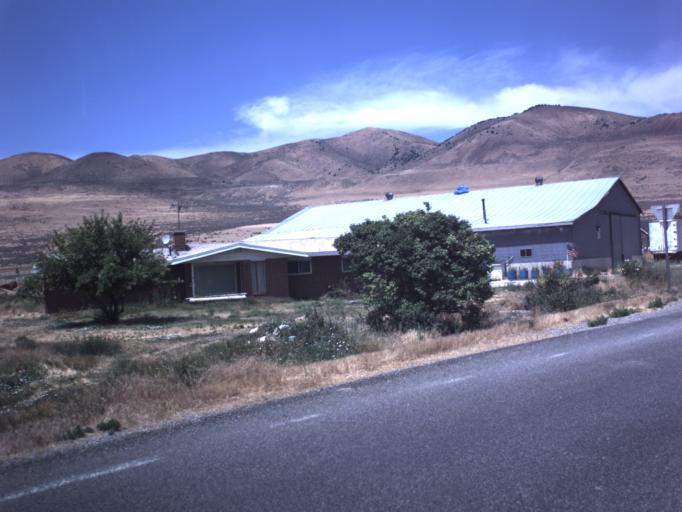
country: US
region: Utah
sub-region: Box Elder County
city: Tremonton
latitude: 41.6502
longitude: -112.3143
